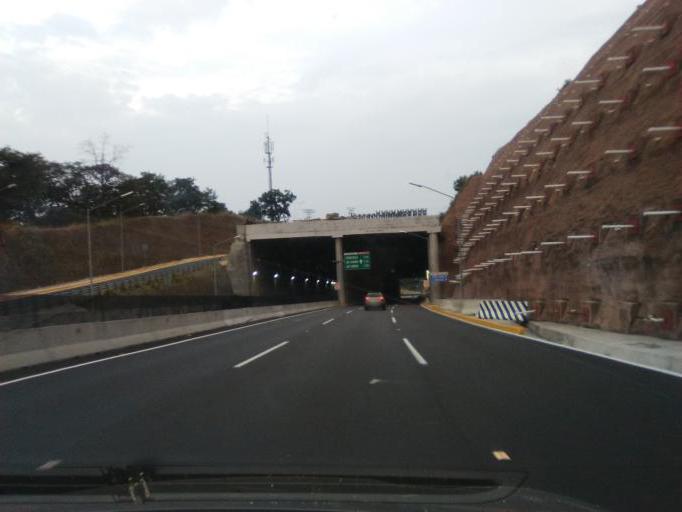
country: MX
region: Mexico City
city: Magdalena Contreras
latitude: 19.3355
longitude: -99.2397
